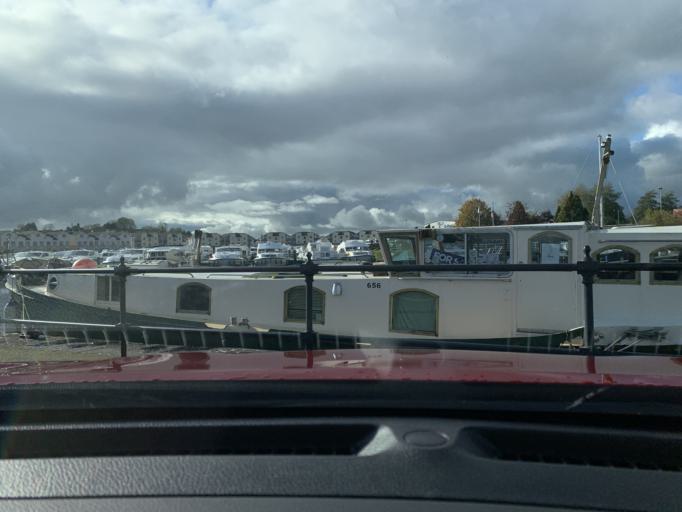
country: IE
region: Connaught
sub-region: County Leitrim
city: Carrick-on-Shannon
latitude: 53.9436
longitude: -8.0963
